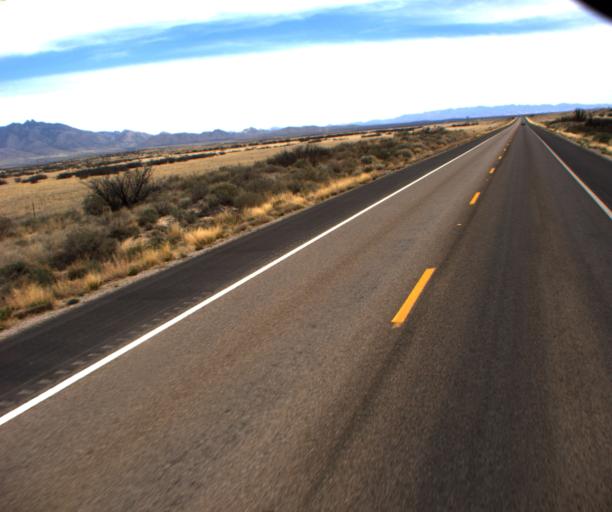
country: US
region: Arizona
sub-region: Cochise County
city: Willcox
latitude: 32.2267
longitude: -109.7968
